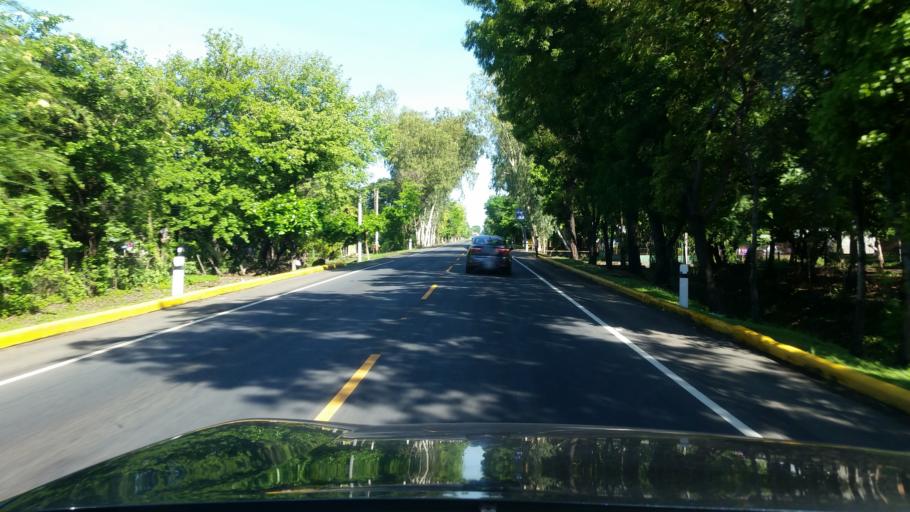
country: NI
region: Chinandega
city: Chichigalpa
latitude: 12.5884
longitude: -87.0168
